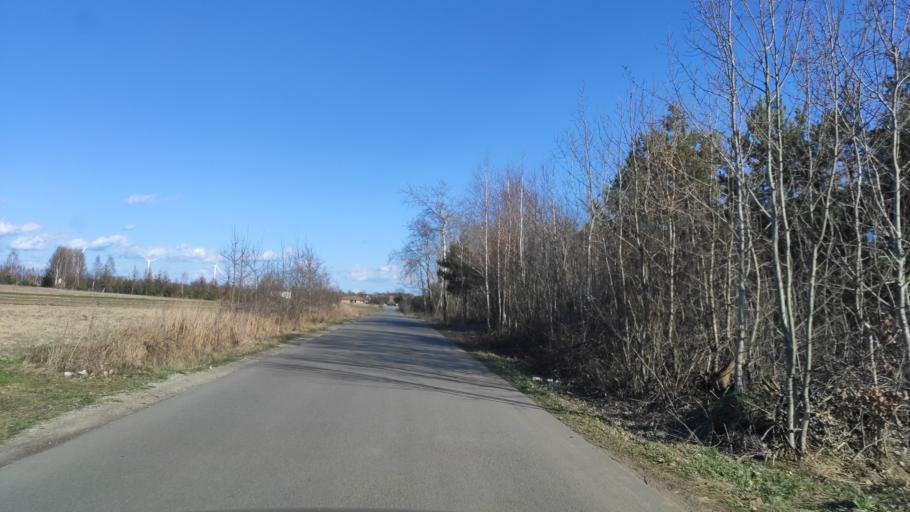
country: PL
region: Masovian Voivodeship
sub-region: Powiat radomski
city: Jastrzebia
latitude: 51.4529
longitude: 21.2356
